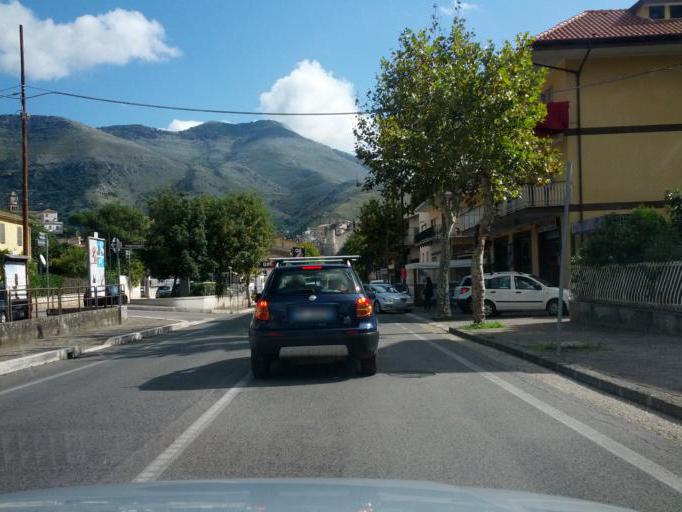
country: IT
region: Latium
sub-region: Provincia di Latina
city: Itri
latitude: 41.2900
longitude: 13.5228
